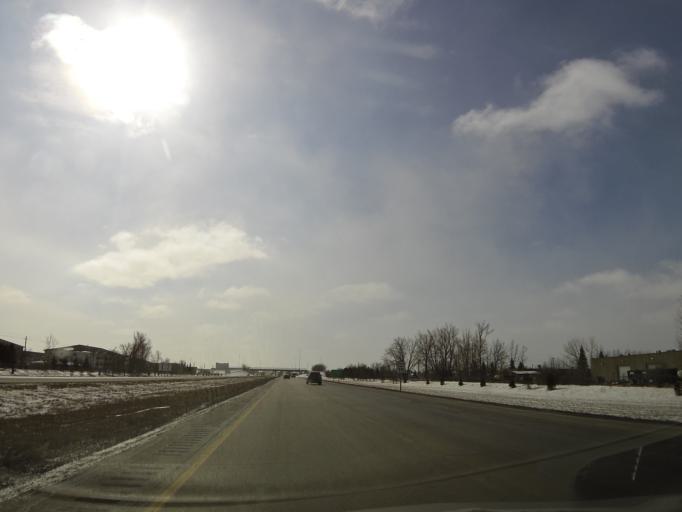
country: US
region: North Dakota
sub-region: Grand Forks County
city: Grand Forks
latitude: 47.9278
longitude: -97.0937
